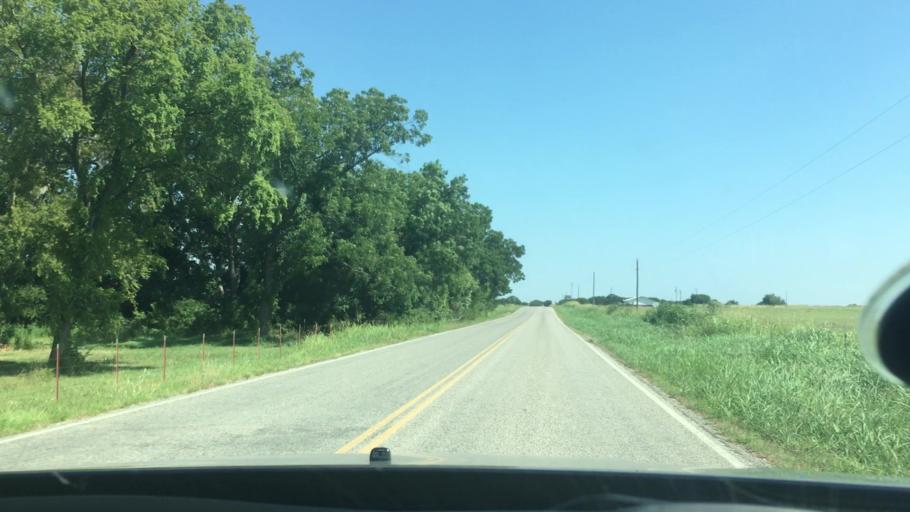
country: US
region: Oklahoma
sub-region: Johnston County
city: Tishomingo
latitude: 34.3067
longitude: -96.6184
